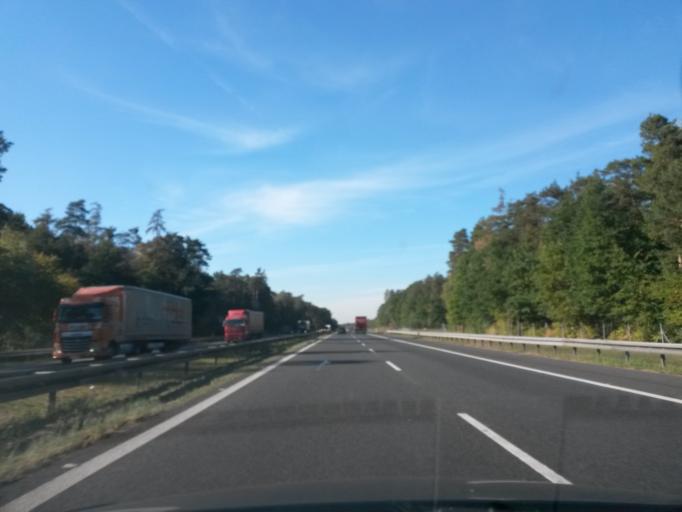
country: PL
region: Opole Voivodeship
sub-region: Powiat brzeski
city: Lewin Brzeski
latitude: 50.6955
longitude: 17.6250
